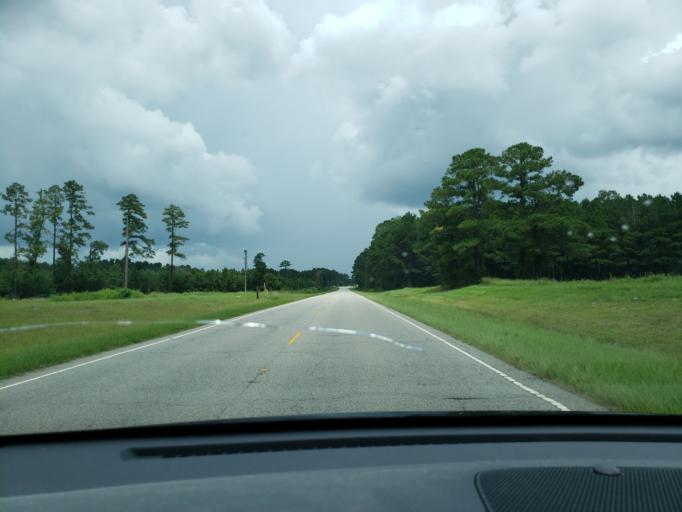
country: US
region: North Carolina
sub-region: Bladen County
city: Bladenboro
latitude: 34.4785
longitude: -78.6664
